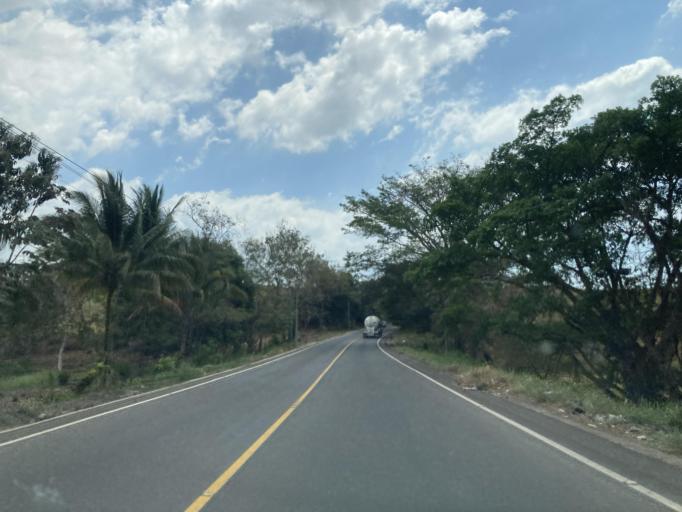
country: GT
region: Santa Rosa
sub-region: Municipio de Taxisco
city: Taxisco
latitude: 14.0836
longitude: -90.4914
